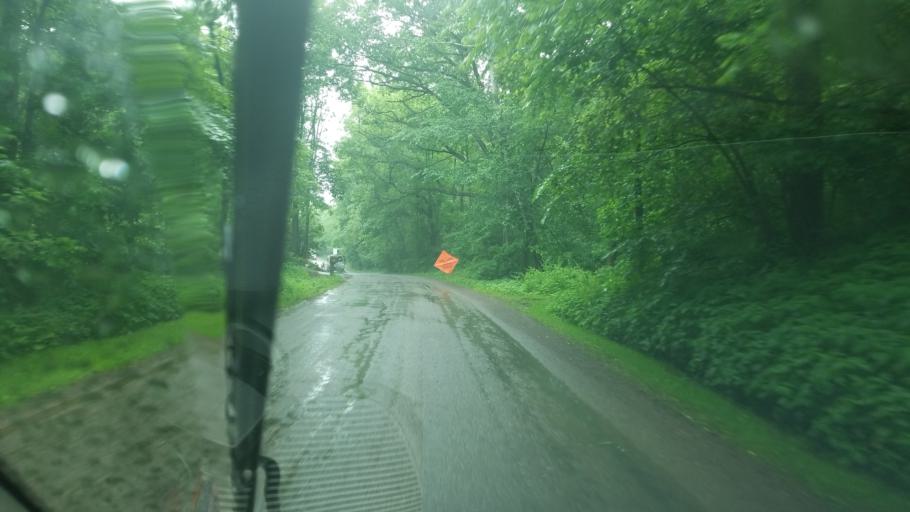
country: US
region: Ohio
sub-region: Sandusky County
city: Bellville
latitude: 40.6092
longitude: -82.4359
